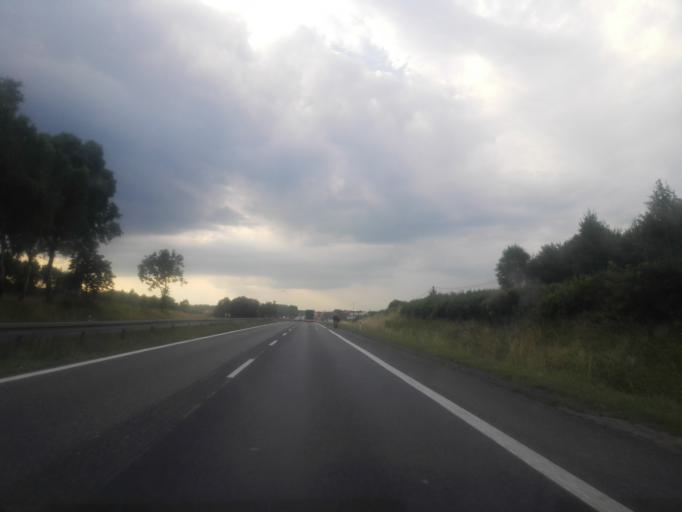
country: PL
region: Silesian Voivodeship
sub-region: Powiat myszkowski
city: Kozieglowy
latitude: 50.6252
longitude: 19.1433
